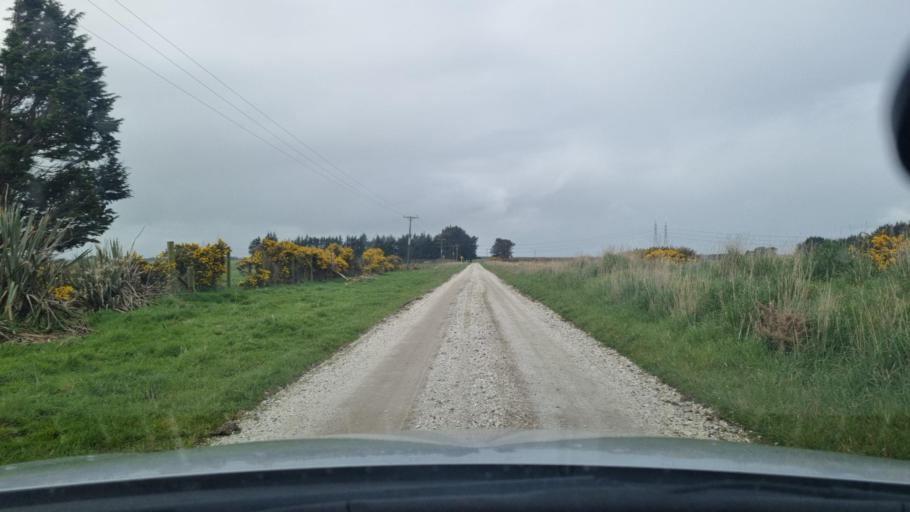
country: NZ
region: Southland
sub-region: Invercargill City
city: Invercargill
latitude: -46.4939
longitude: 168.4243
